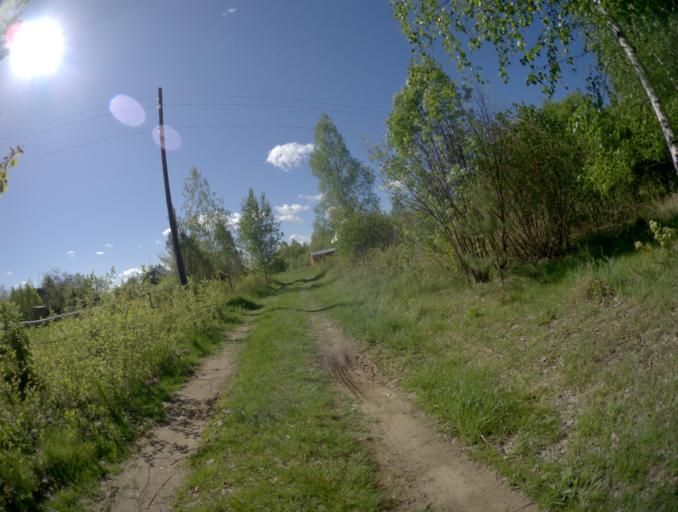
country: RU
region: Rjazan
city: Spas-Klepiki
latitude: 55.2474
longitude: 40.0989
